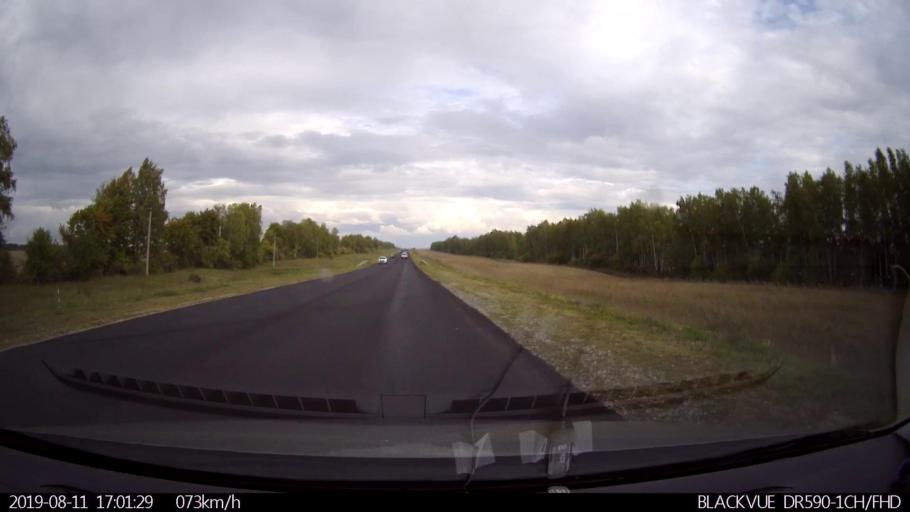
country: RU
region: Ulyanovsk
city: Mayna
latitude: 54.3083
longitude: 47.6980
